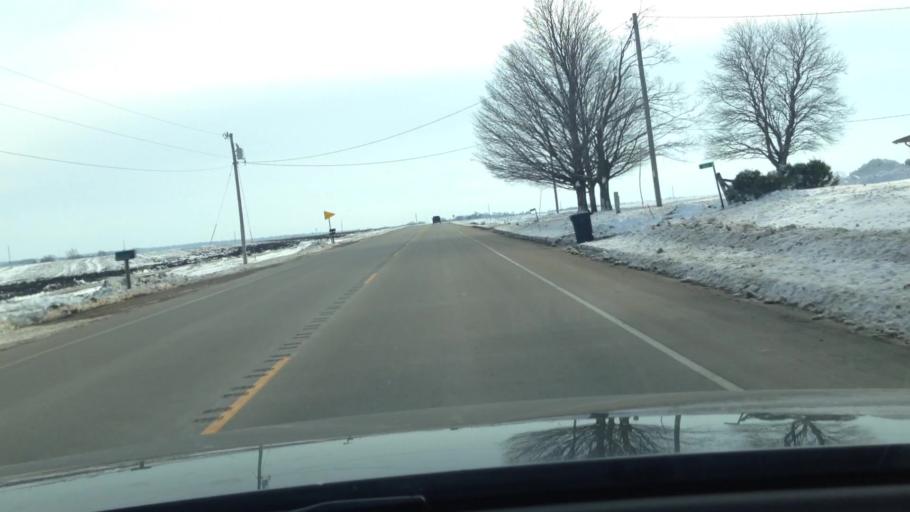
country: US
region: Illinois
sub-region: McHenry County
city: Hebron
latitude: 42.5237
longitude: -88.4428
